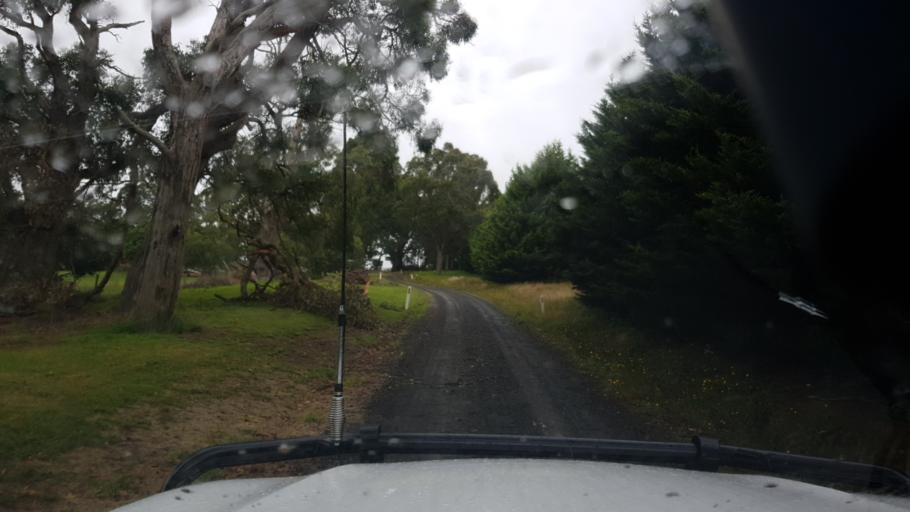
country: AU
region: Victoria
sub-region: Baw Baw
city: Warragul
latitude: -38.1140
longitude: 145.8907
